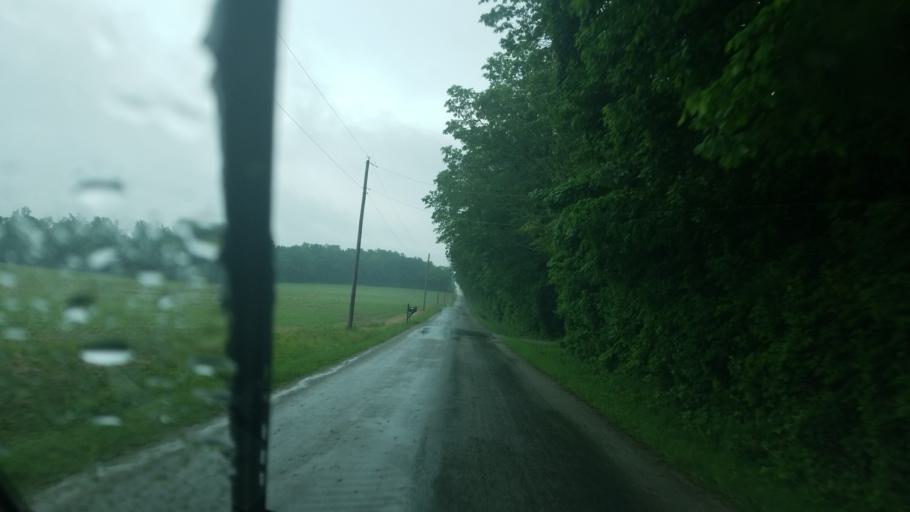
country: US
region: Ohio
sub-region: Huron County
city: Plymouth
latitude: 40.9451
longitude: -82.7211
